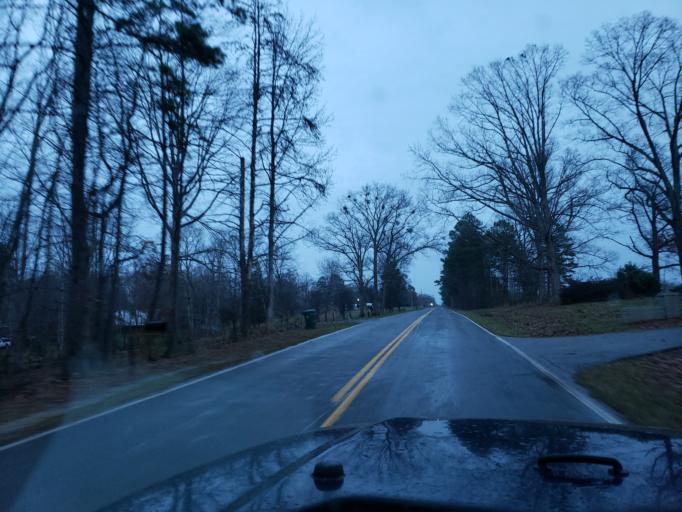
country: US
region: South Carolina
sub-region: Cherokee County
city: Blacksburg
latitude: 35.1455
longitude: -81.4411
